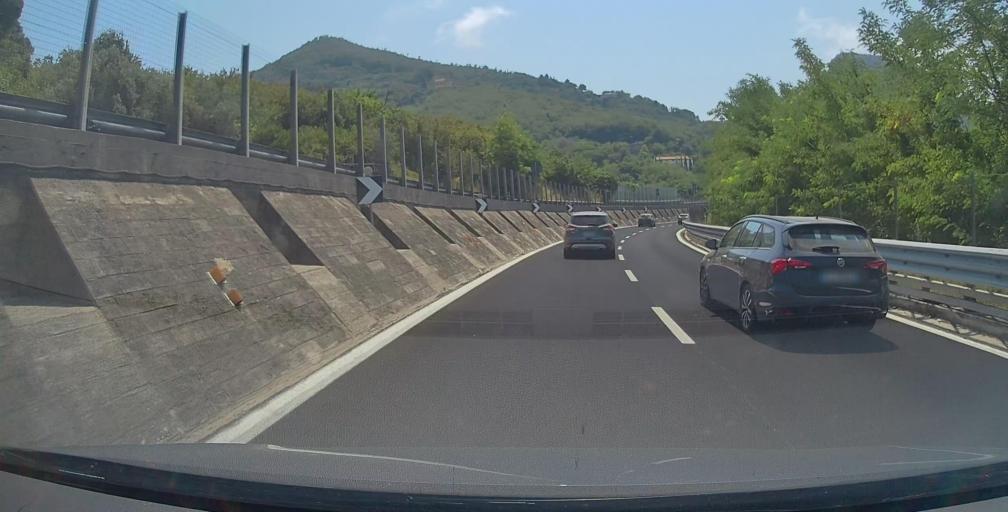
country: IT
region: Campania
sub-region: Provincia di Salerno
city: Dragonea
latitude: 40.6913
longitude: 14.7214
